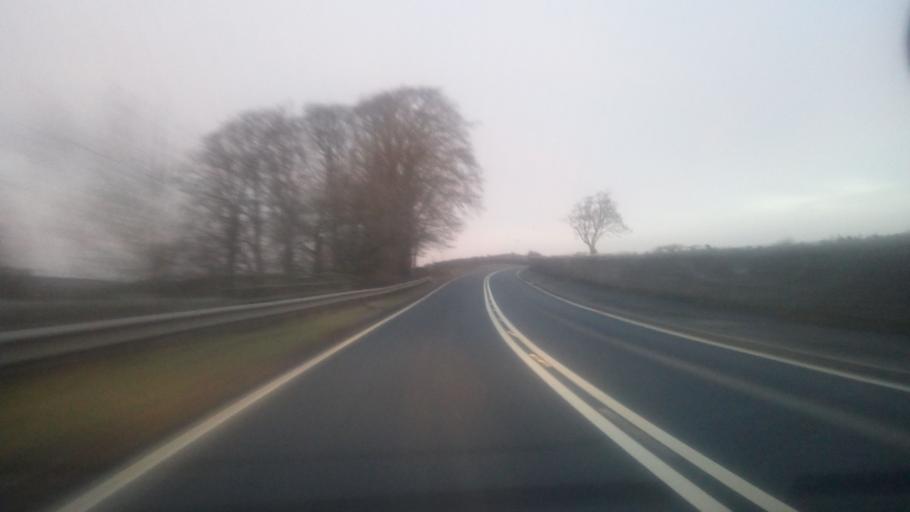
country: GB
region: Scotland
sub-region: The Scottish Borders
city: Lauder
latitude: 55.7268
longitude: -2.7621
